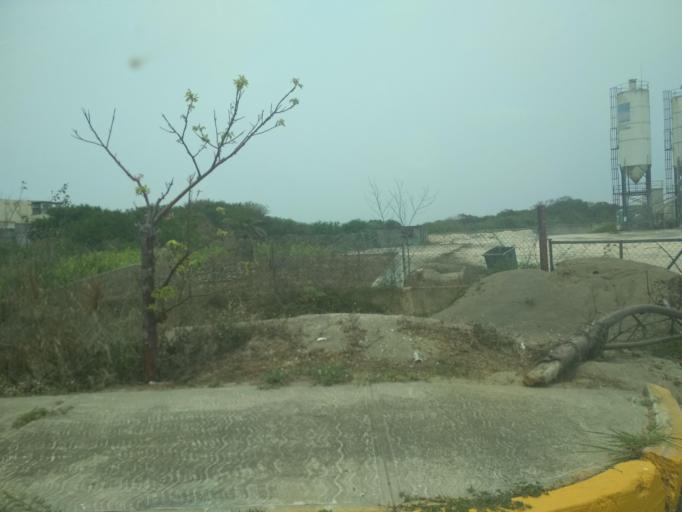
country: MX
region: Veracruz
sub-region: Alvarado
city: Playa de la Libertad
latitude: 19.0612
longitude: -96.0730
